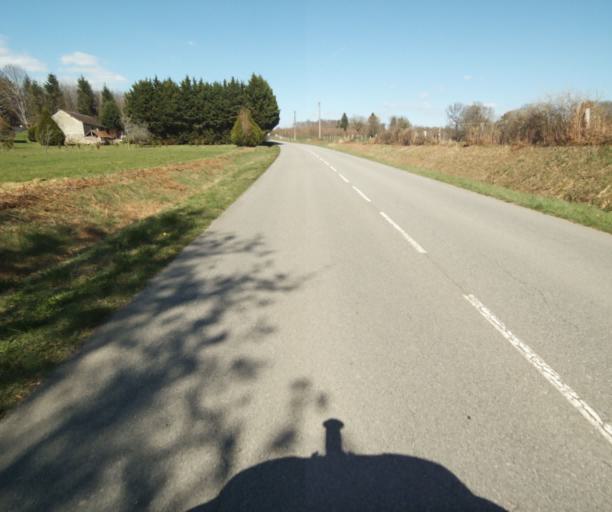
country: FR
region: Limousin
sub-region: Departement de la Correze
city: Saint-Mexant
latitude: 45.2957
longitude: 1.6705
